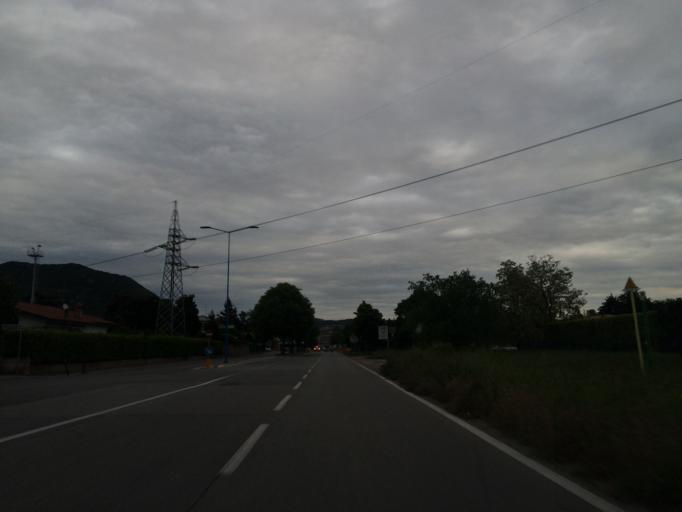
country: IT
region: Lombardy
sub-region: Provincia di Brescia
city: Buffalora-Bettole
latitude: 45.5145
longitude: 10.2600
